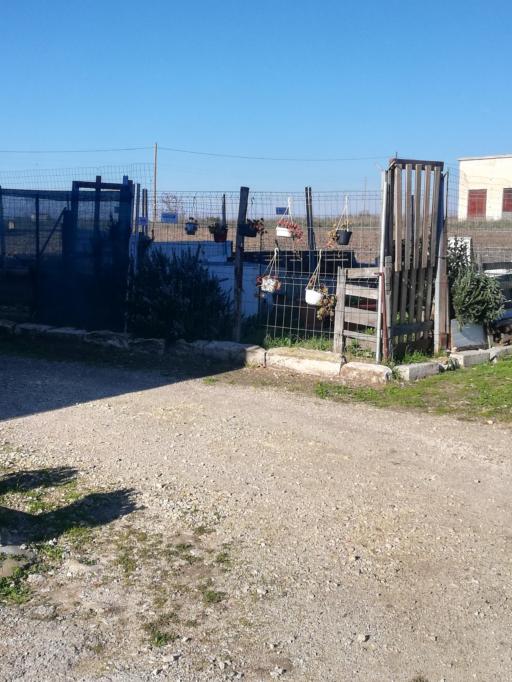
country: IT
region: Apulia
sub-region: Provincia di Bari
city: Poggiorsini
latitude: 40.8564
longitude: 16.3306
